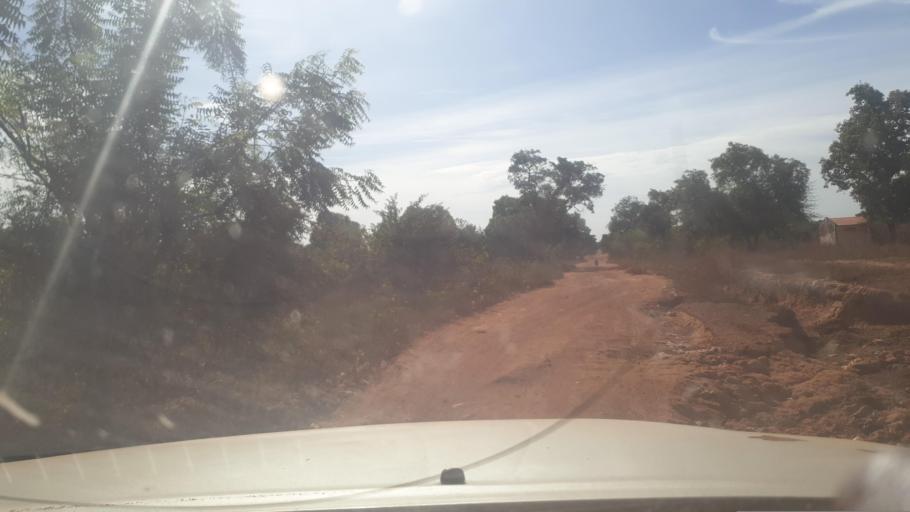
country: ML
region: Sikasso
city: Sikasso
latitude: 11.8394
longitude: -6.0103
